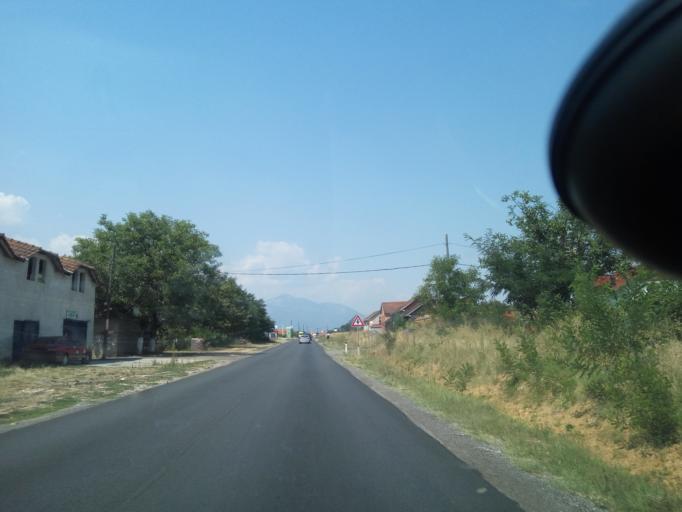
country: XK
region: Gjakova
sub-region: Komuna e Decanit
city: Gllogjan
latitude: 42.4420
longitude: 20.3668
